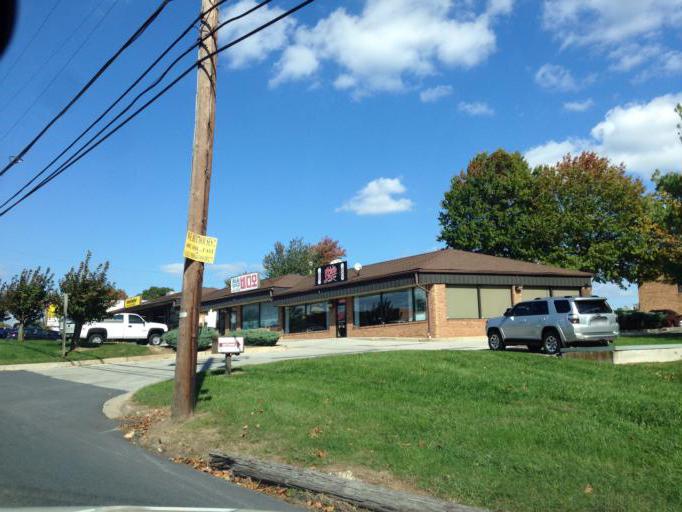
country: US
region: Maryland
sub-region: Howard County
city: Ellicott City
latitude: 39.2762
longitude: -76.8320
